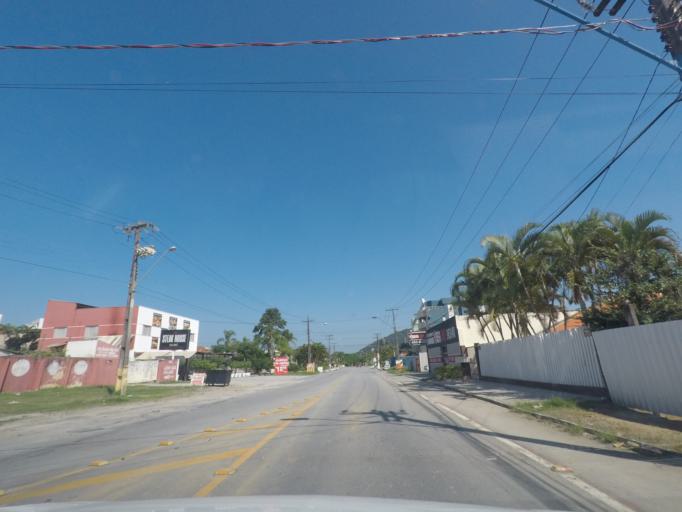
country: BR
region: Parana
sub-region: Guaratuba
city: Guaratuba
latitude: -25.8311
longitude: -48.5394
